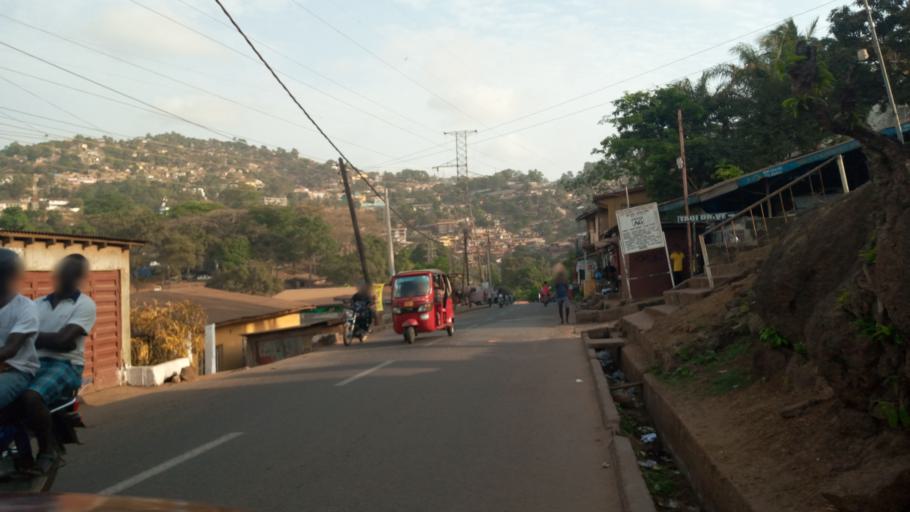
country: SL
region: Western Area
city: Freetown
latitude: 8.4727
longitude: -13.2518
